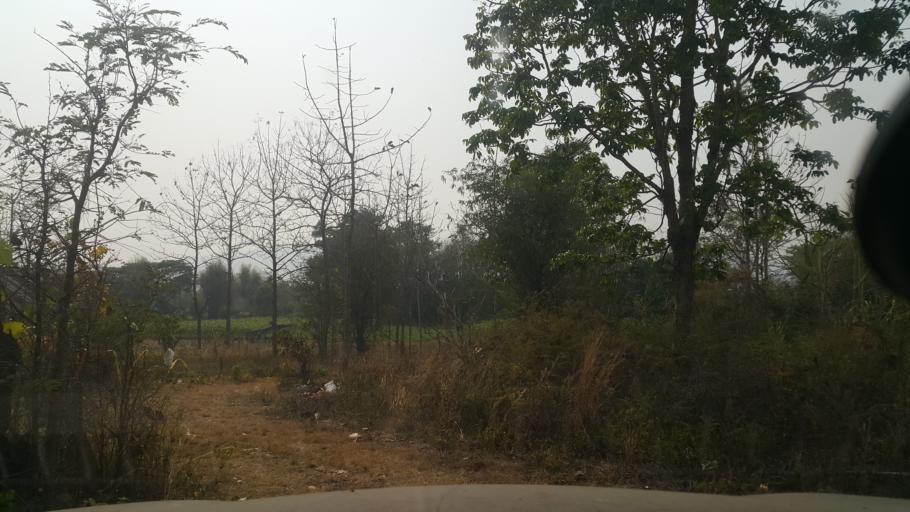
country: TH
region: Chiang Mai
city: Mae On
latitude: 18.7645
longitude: 99.2693
